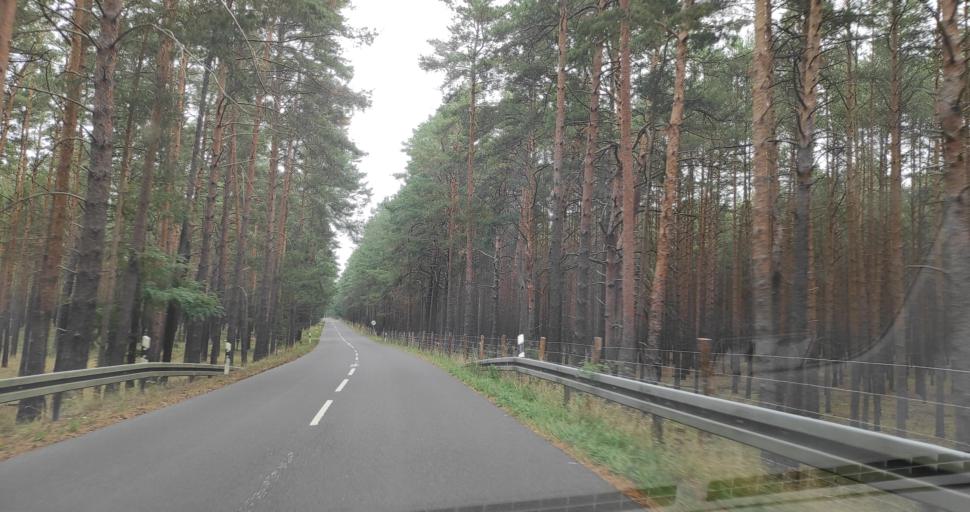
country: DE
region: Brandenburg
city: Forst
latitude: 51.7101
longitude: 14.5496
